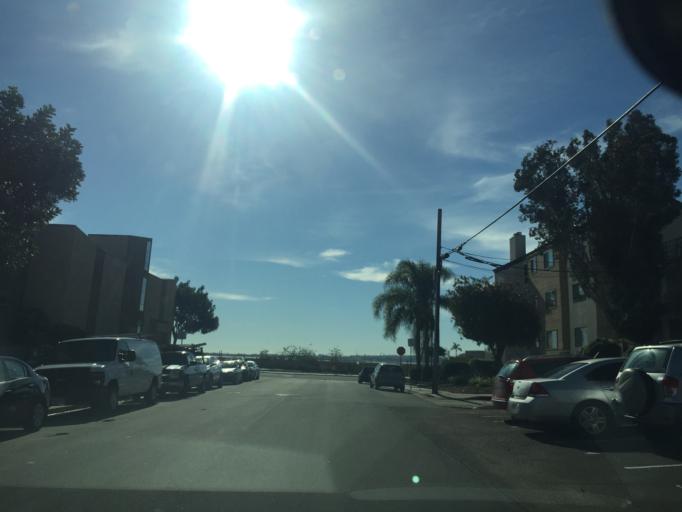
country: US
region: California
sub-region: San Diego County
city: La Jolla
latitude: 32.7968
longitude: -117.2302
